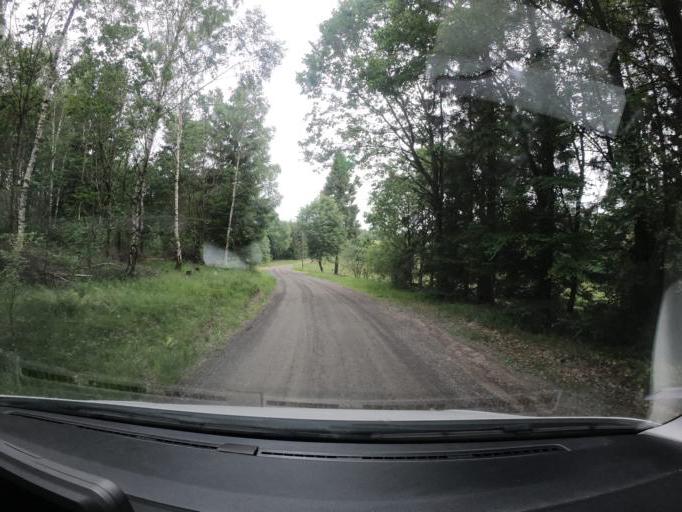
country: SE
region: Skane
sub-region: Hoors Kommun
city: Hoeoer
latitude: 55.9942
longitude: 13.4770
